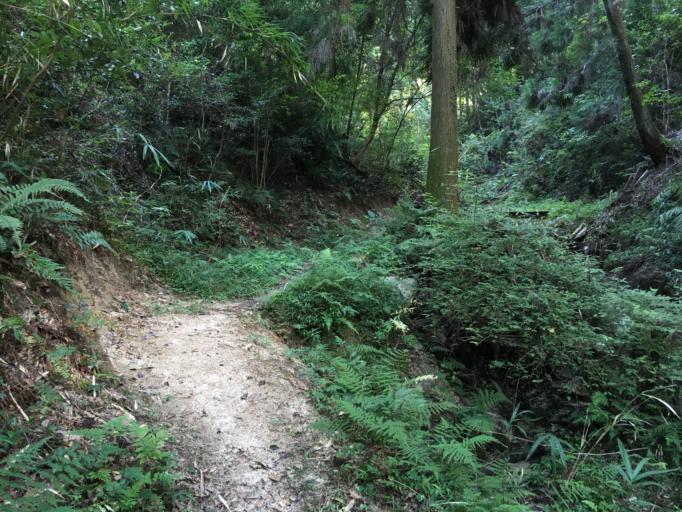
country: JP
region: Osaka
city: Neyagawa
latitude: 34.7469
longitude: 135.6859
